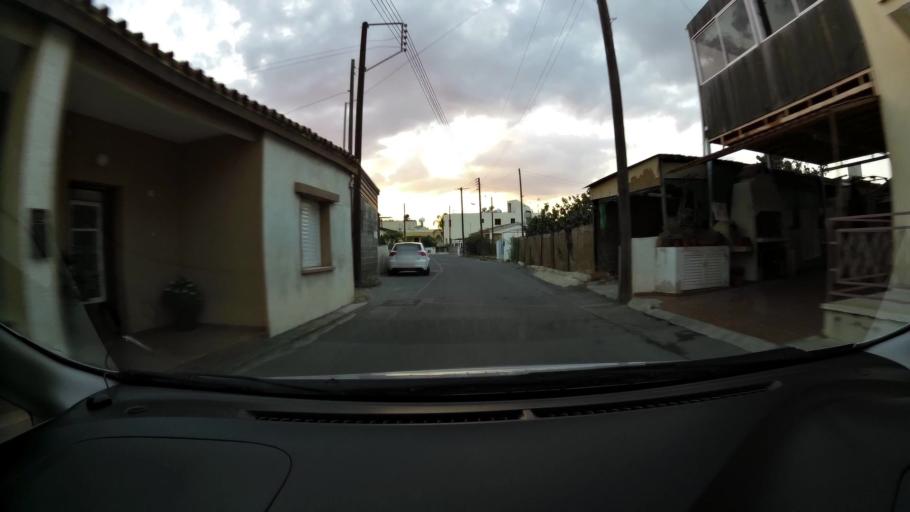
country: CY
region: Larnaka
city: Dhromolaxia
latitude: 34.8772
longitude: 33.5844
